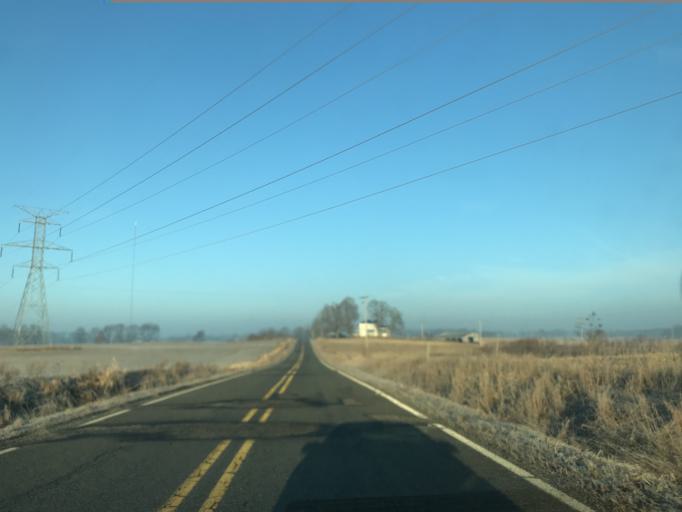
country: US
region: Michigan
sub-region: Ingham County
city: Leslie
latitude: 42.4154
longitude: -84.5058
